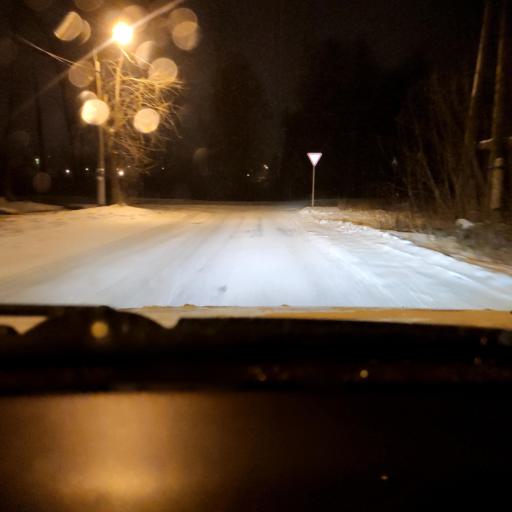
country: RU
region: Perm
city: Polazna
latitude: 58.1318
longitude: 56.3782
